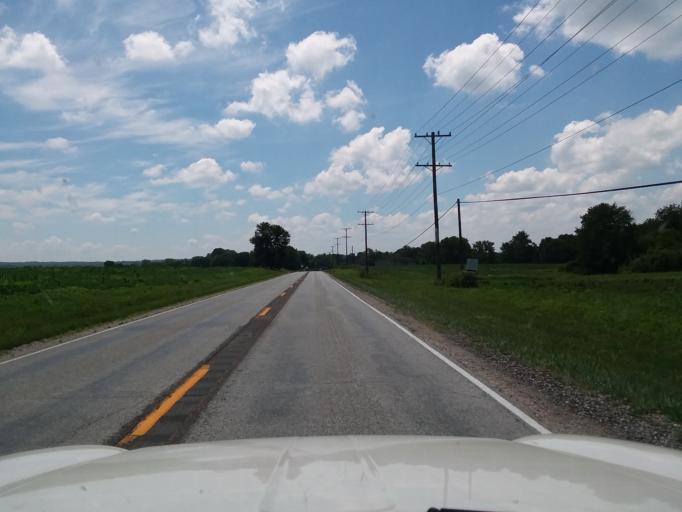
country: US
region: Indiana
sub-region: Johnson County
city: Trafalgar
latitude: 39.3775
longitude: -86.2478
